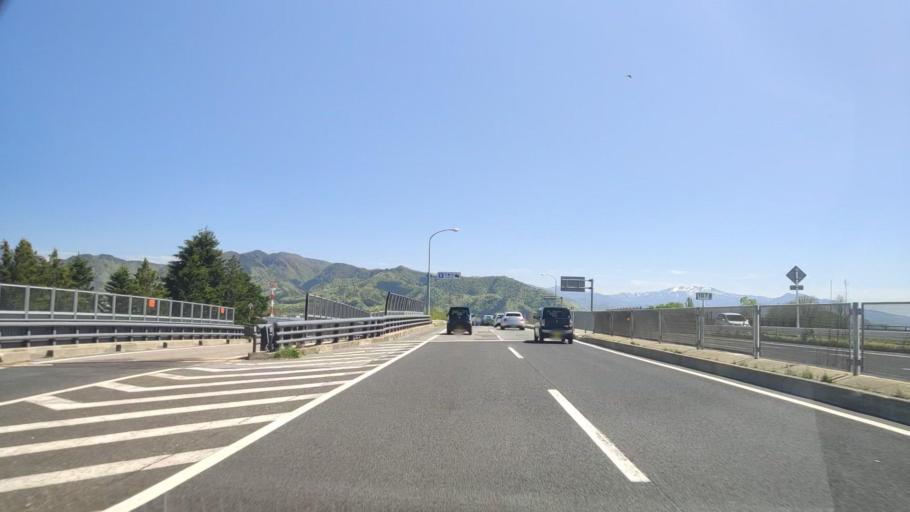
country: JP
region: Yamagata
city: Tendo
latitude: 38.3975
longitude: 140.3759
